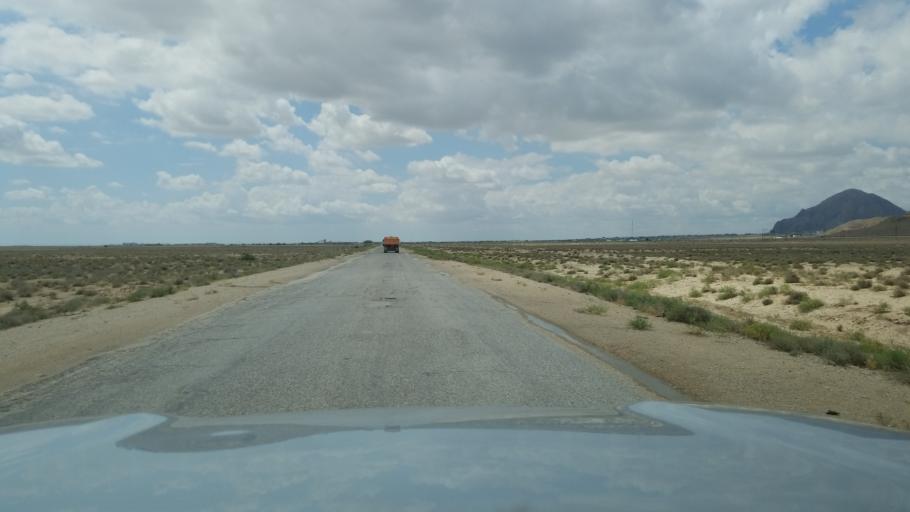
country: TM
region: Balkan
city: Balkanabat
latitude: 39.4841
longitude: 54.4324
